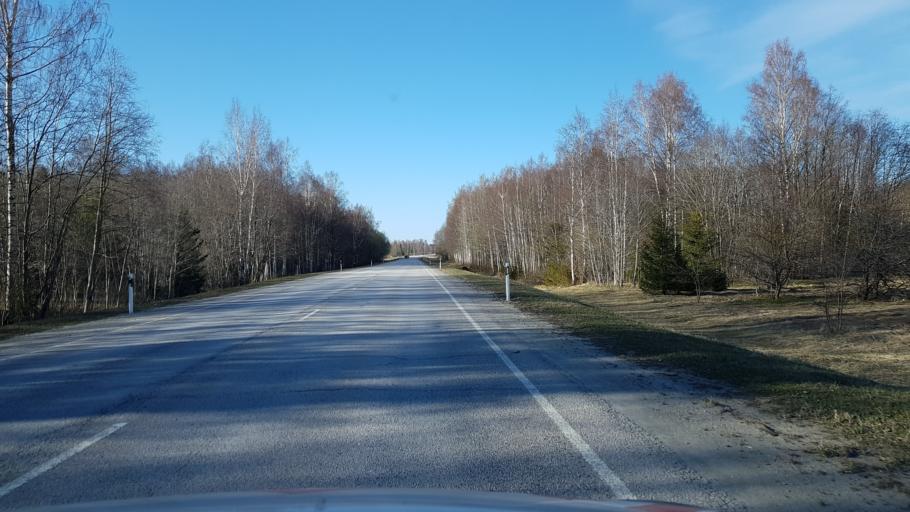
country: EE
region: Ida-Virumaa
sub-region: Johvi vald
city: Johvi
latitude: 59.1795
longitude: 27.3488
